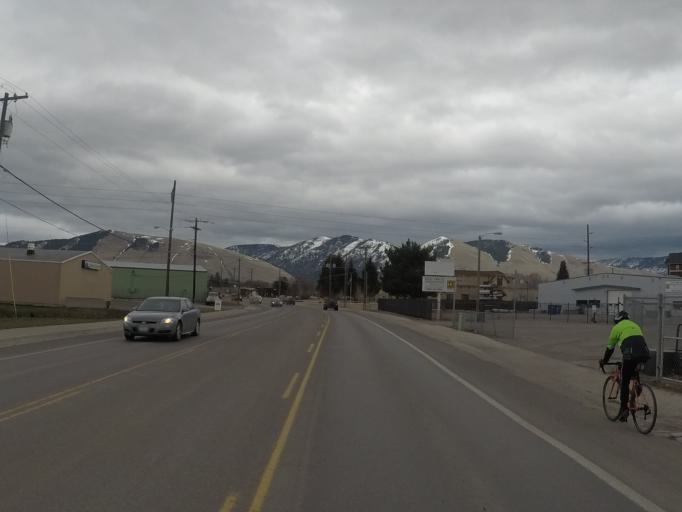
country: US
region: Montana
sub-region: Missoula County
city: Orchard Homes
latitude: 46.8810
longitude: -114.0250
